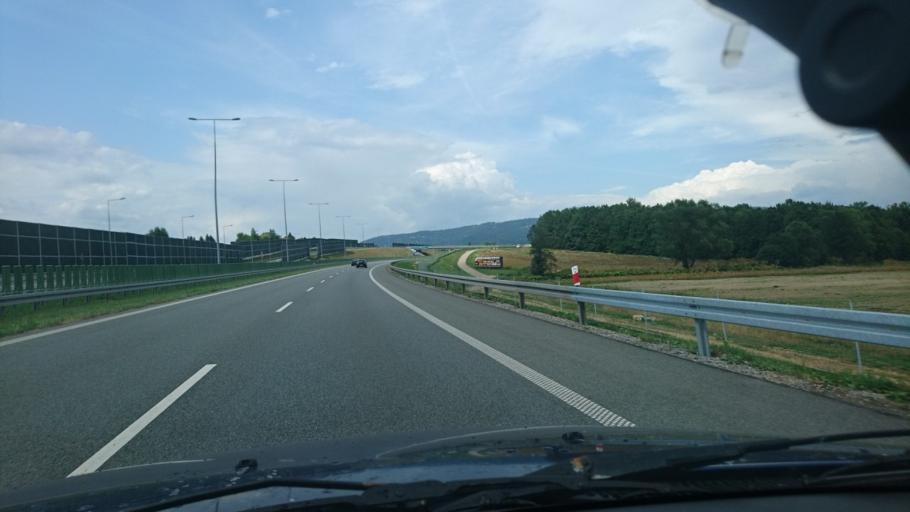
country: PL
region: Silesian Voivodeship
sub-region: Powiat bielski
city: Rybarzowice
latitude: 49.7080
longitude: 19.1207
